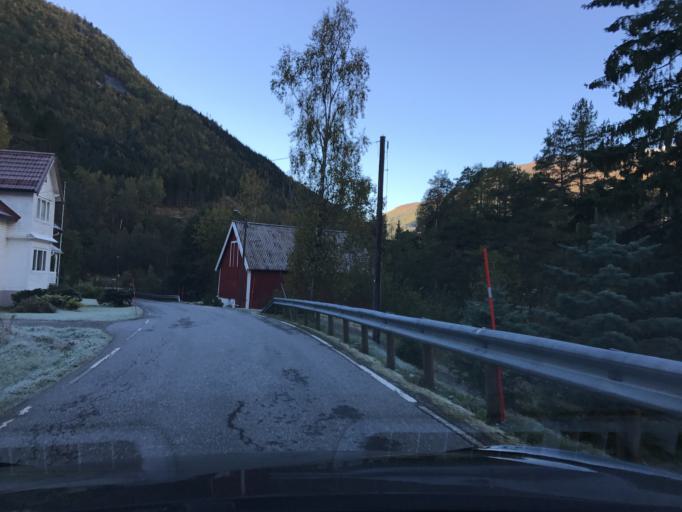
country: NO
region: More og Romsdal
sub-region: Norddal
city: Valldal
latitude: 62.3140
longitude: 7.2922
